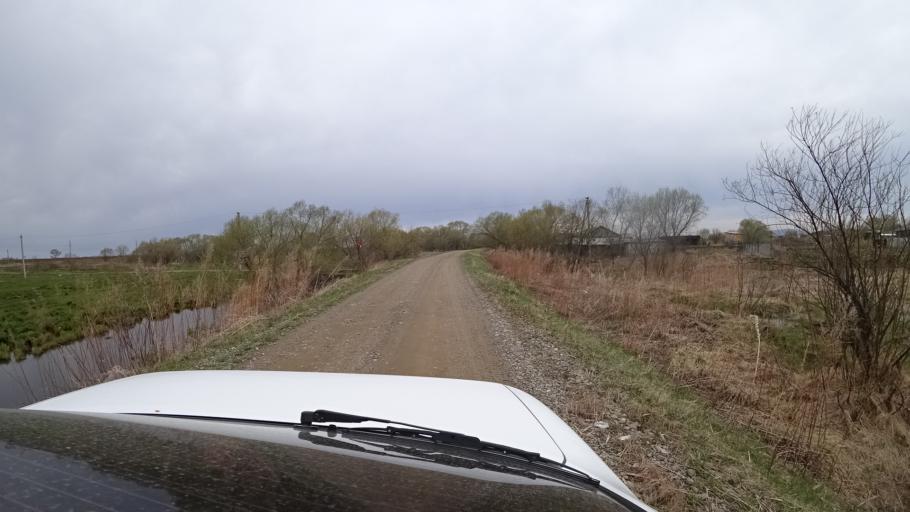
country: RU
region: Primorskiy
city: Dal'nerechensk
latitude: 45.9753
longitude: 133.7518
